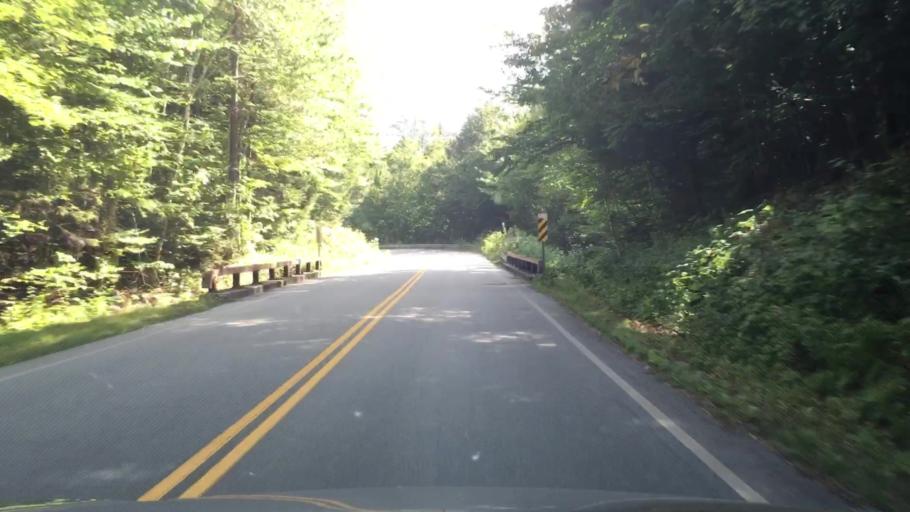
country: US
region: New Hampshire
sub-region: Carroll County
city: Tamworth
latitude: 44.0234
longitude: -71.3214
